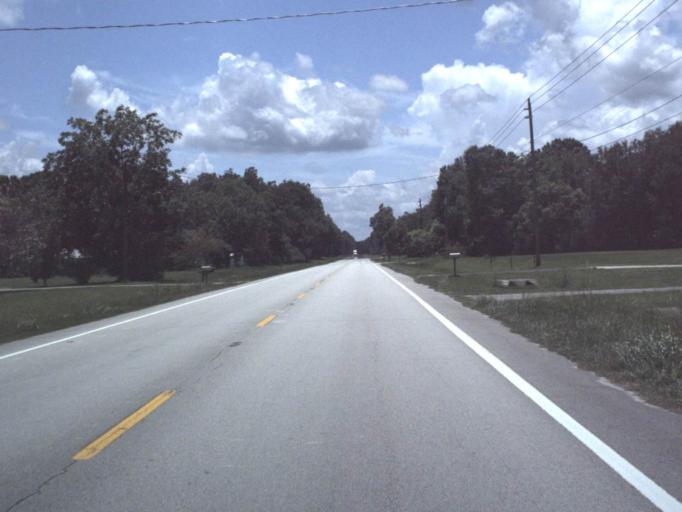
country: US
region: Florida
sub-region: Bradford County
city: Starke
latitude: 30.0114
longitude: -82.1430
